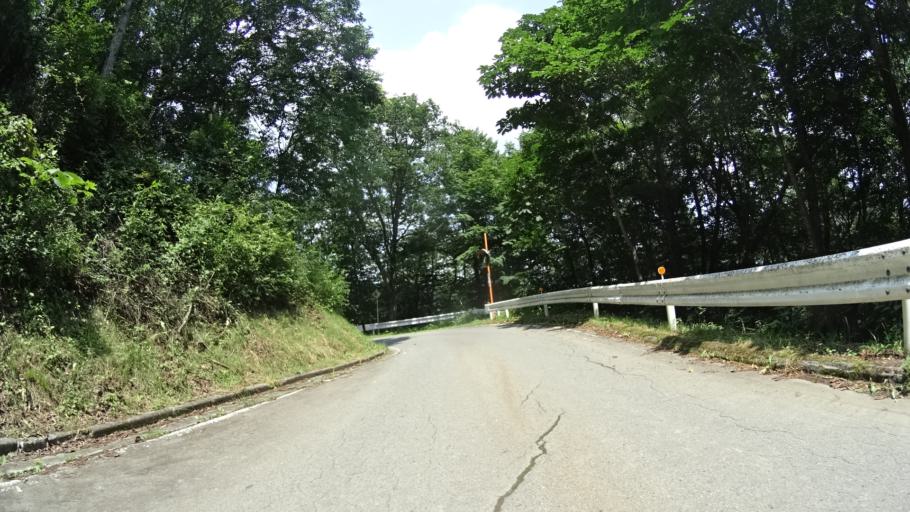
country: JP
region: Nagano
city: Saku
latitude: 36.1020
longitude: 138.6499
